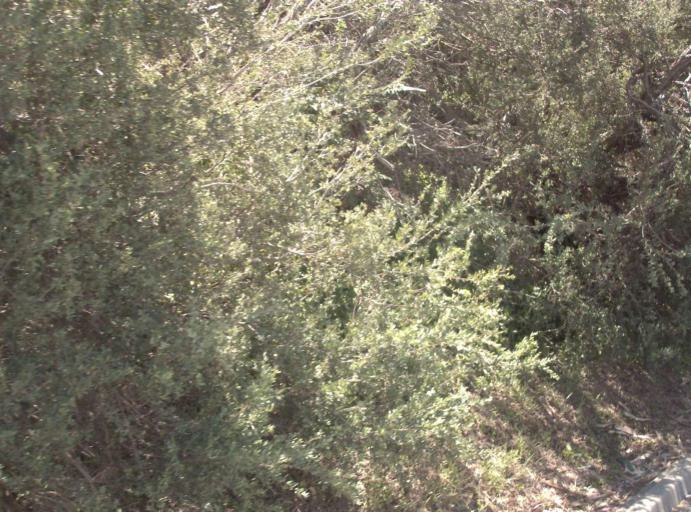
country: AU
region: Victoria
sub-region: Mornington Peninsula
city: Mount Eliza
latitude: -38.1741
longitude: 145.0971
